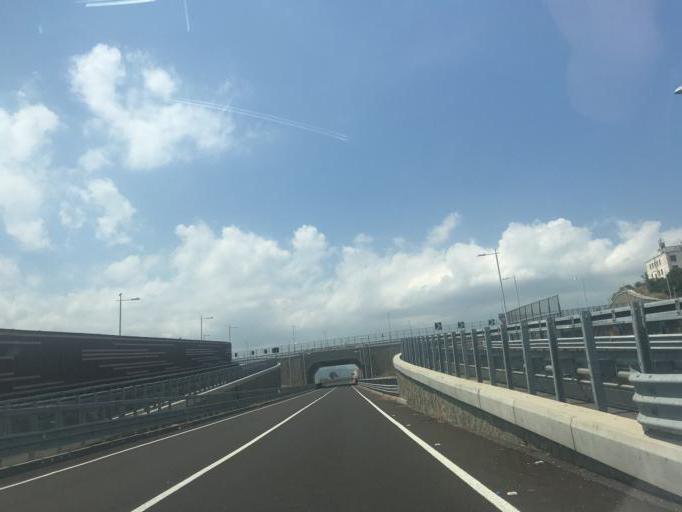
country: IT
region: Sardinia
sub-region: Provincia di Olbia-Tempio
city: Olbia
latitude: 40.9044
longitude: 9.5039
